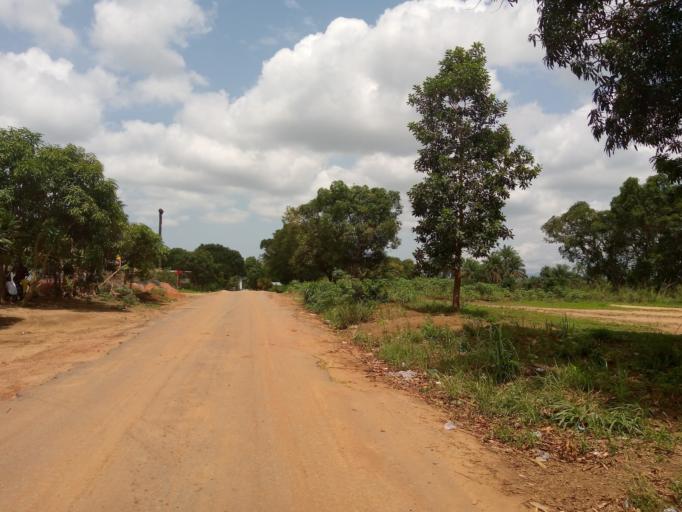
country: SL
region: Western Area
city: Waterloo
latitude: 8.3817
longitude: -12.9583
